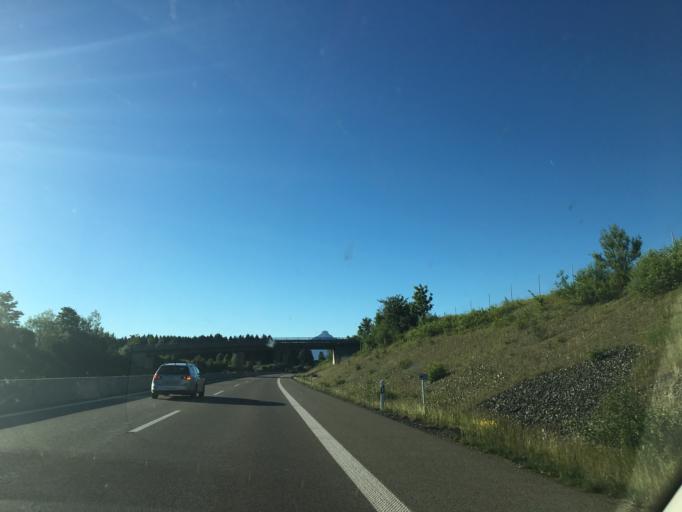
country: DE
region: Bavaria
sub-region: Swabia
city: Ruckholz
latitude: 47.6379
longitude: 10.5604
